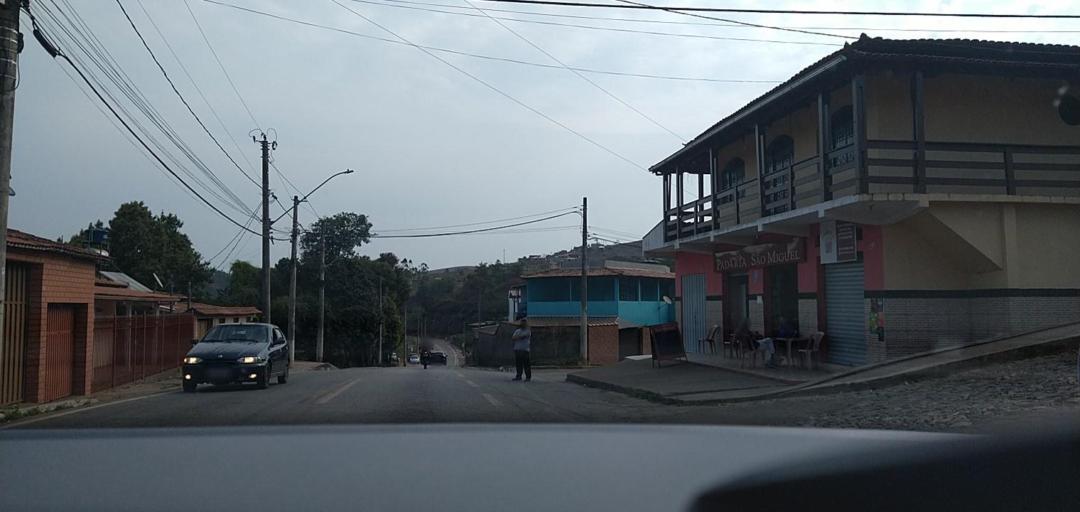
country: BR
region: Minas Gerais
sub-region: Rio Piracicaba
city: Rio Piracicaba
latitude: -19.9014
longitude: -43.1472
